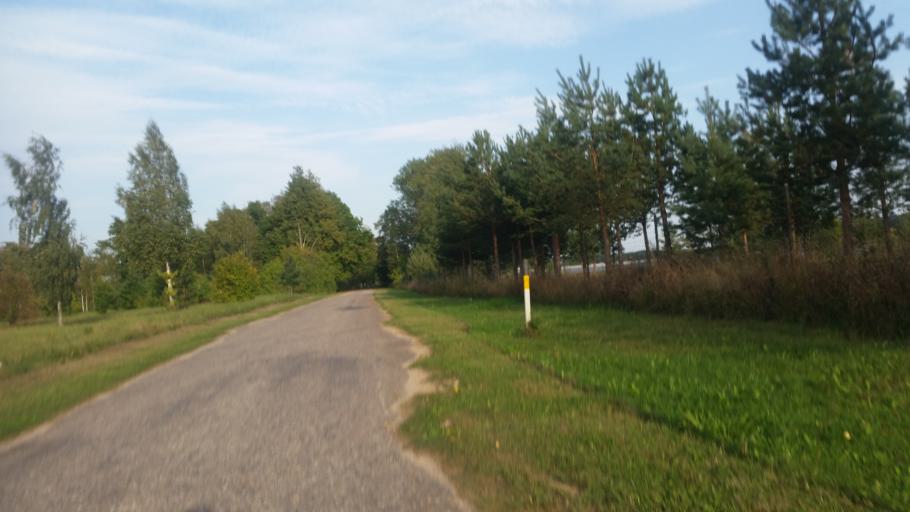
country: LV
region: Ikskile
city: Ikskile
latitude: 56.8179
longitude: 24.5524
